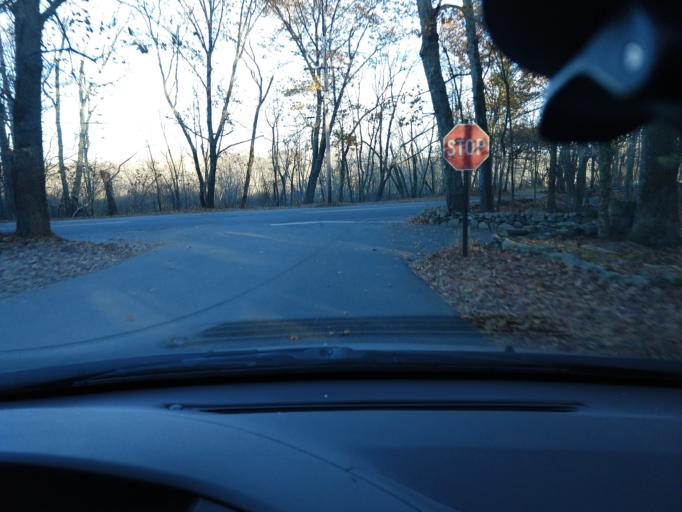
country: US
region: Massachusetts
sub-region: Middlesex County
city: Carlisle
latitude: 42.5101
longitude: -71.3159
